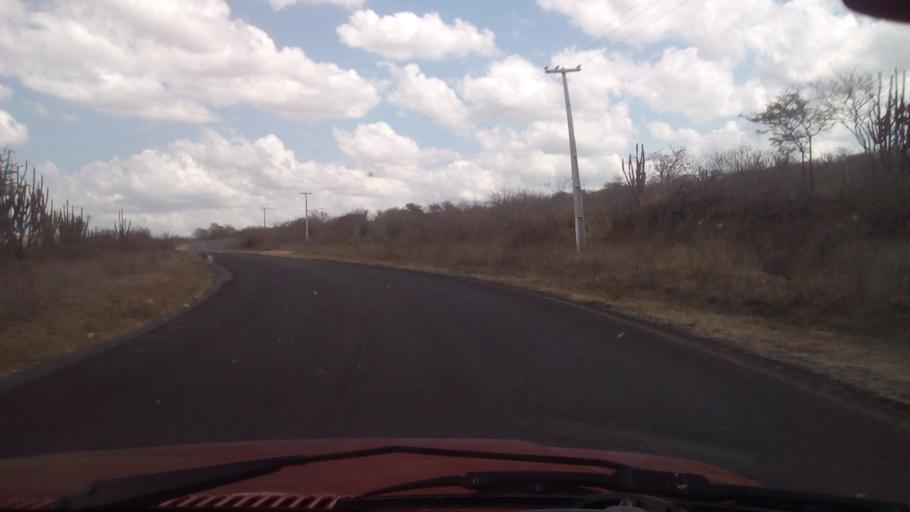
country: BR
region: Paraiba
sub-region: Cacimba De Dentro
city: Cacimba de Dentro
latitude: -6.6910
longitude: -35.7439
